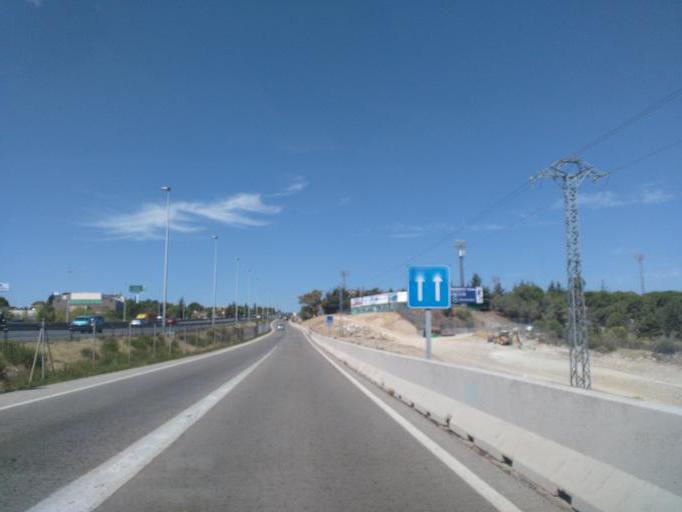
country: ES
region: Madrid
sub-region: Provincia de Madrid
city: Torrelodones
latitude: 40.5703
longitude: -3.9198
